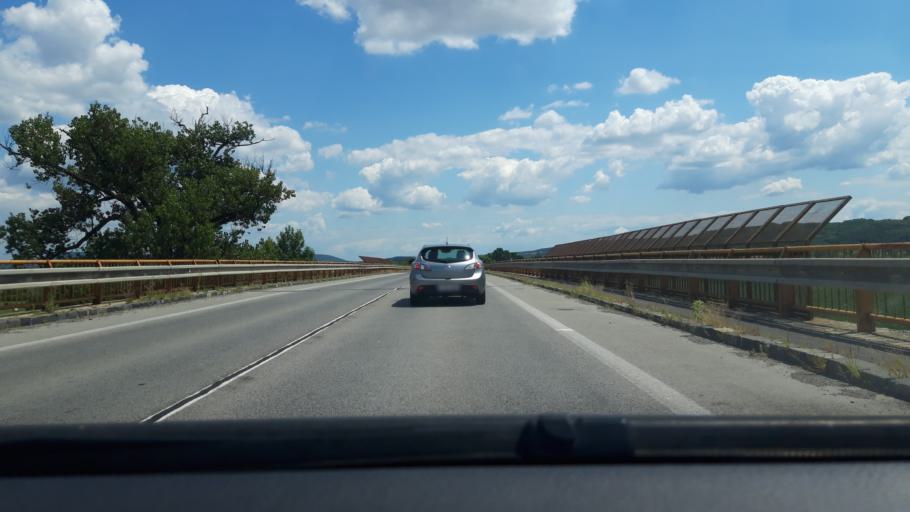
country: SK
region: Banskobystricky
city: Lucenec
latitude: 48.3082
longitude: 19.7152
